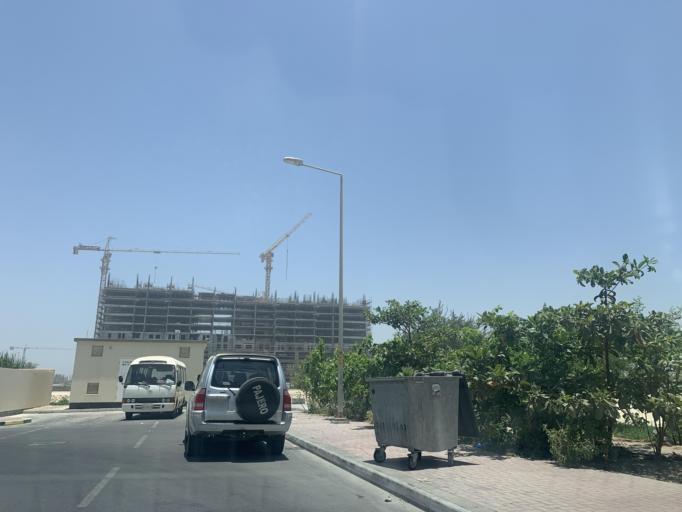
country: BH
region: Manama
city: Jidd Hafs
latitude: 26.2360
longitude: 50.4588
